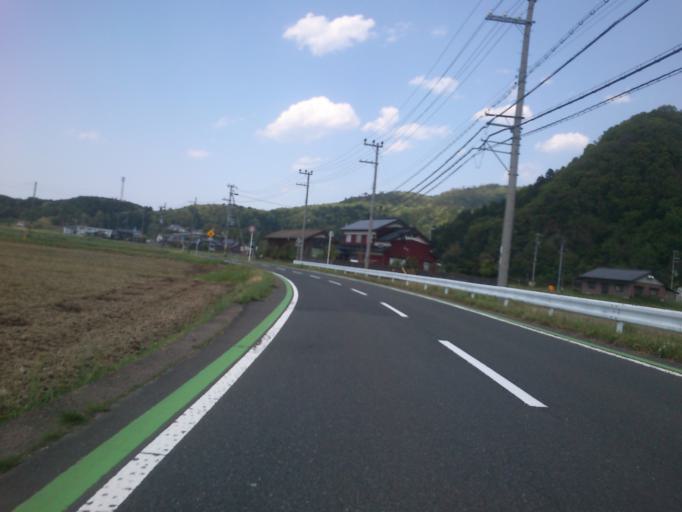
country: JP
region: Kyoto
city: Miyazu
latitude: 35.7179
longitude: 135.1081
